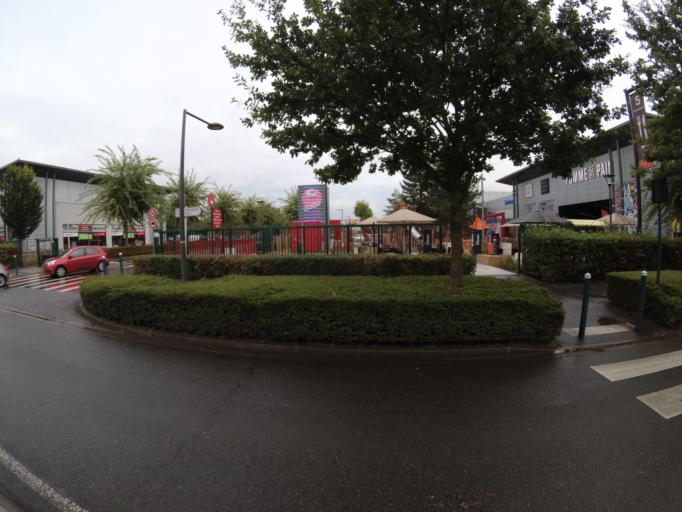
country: FR
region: Ile-de-France
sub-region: Departement de Seine-et-Marne
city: Chanteloup-en-Brie
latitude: 48.8558
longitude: 2.7533
